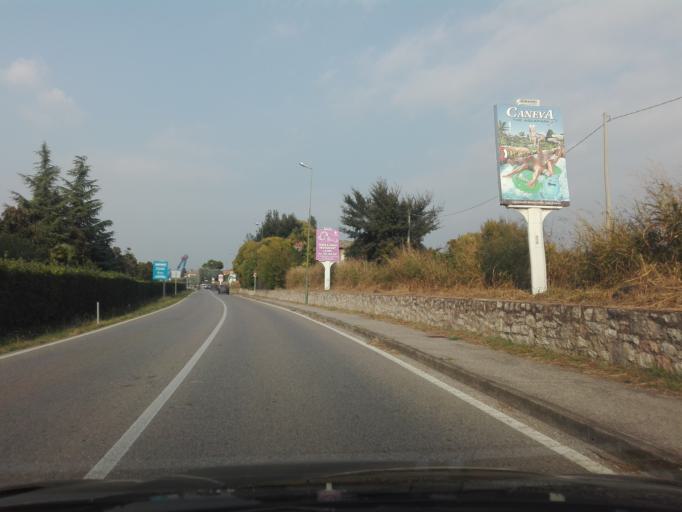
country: IT
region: Veneto
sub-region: Provincia di Verona
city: Cola
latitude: 45.4712
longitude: 10.7236
